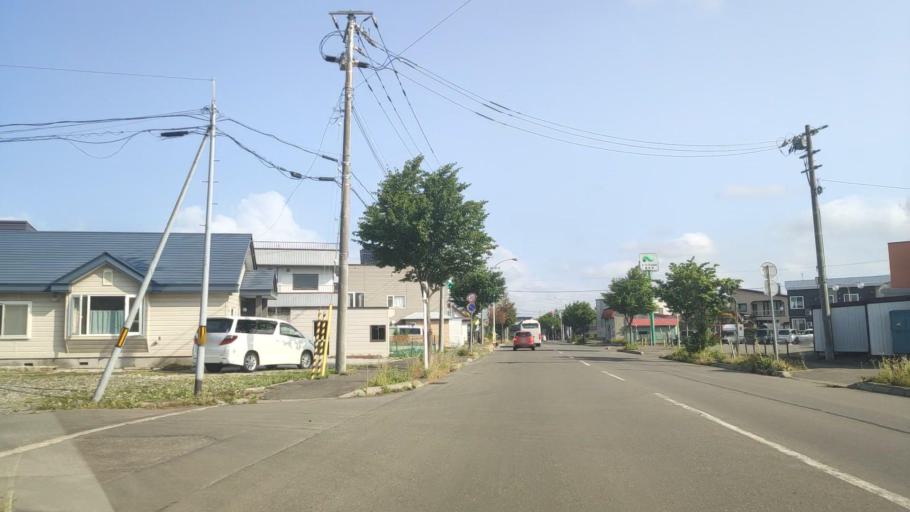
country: JP
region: Hokkaido
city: Shimo-furano
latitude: 43.3425
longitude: 142.3954
